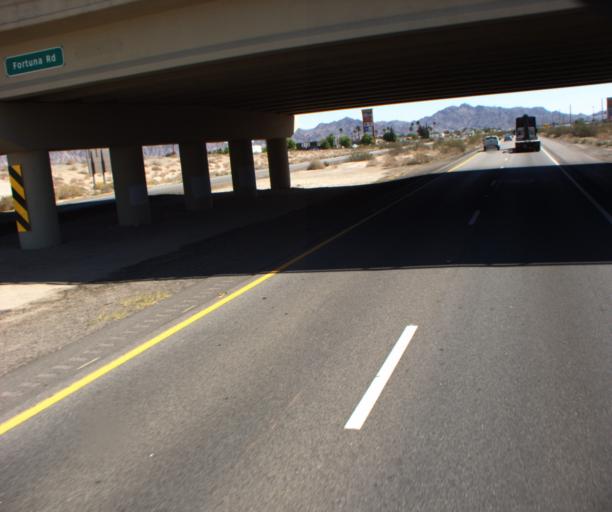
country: US
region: Arizona
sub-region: Yuma County
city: Fortuna Foothills
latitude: 32.6704
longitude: -114.4445
